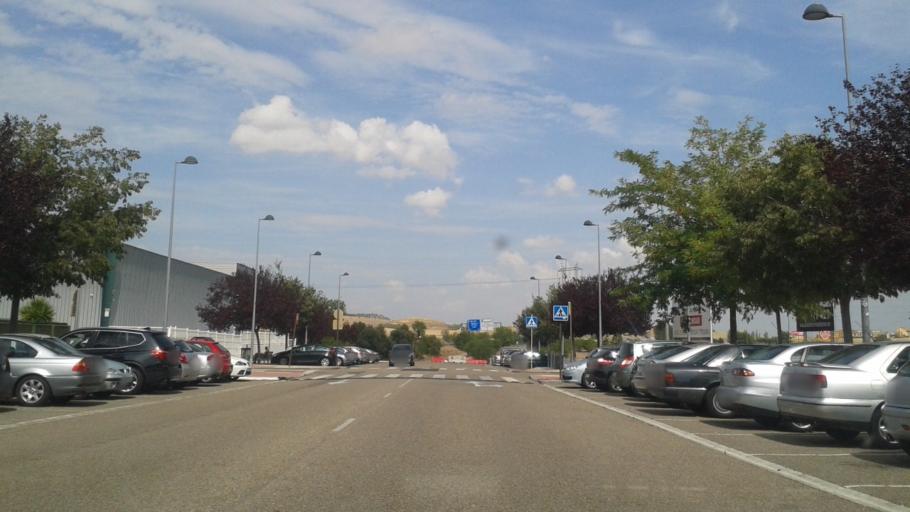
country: ES
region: Castille and Leon
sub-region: Provincia de Valladolid
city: Arroyo
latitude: 41.6291
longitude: -4.7771
